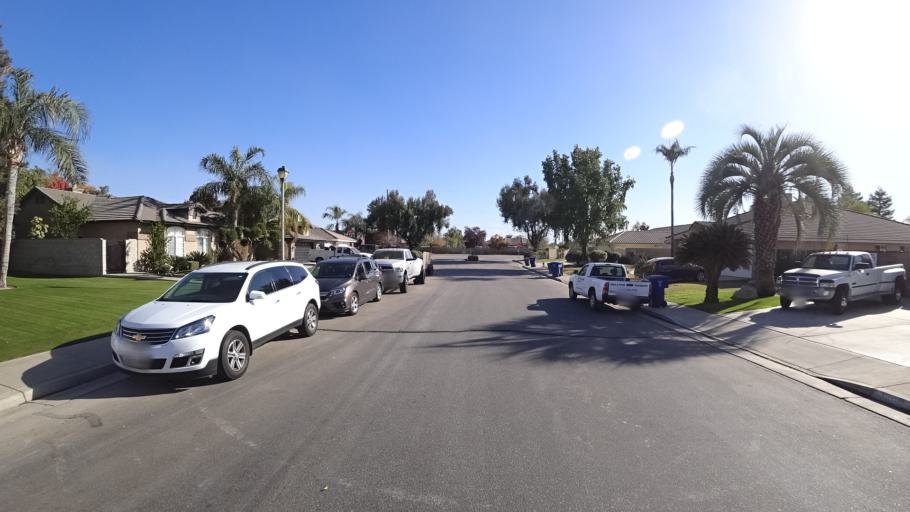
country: US
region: California
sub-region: Kern County
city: Greenfield
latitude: 35.2759
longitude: -119.0400
